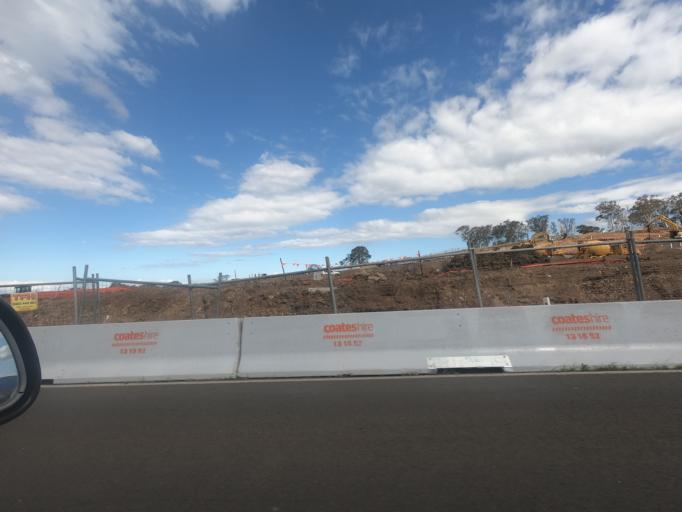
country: AU
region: New South Wales
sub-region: Wollongong
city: Dapto
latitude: -34.4762
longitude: 150.7877
